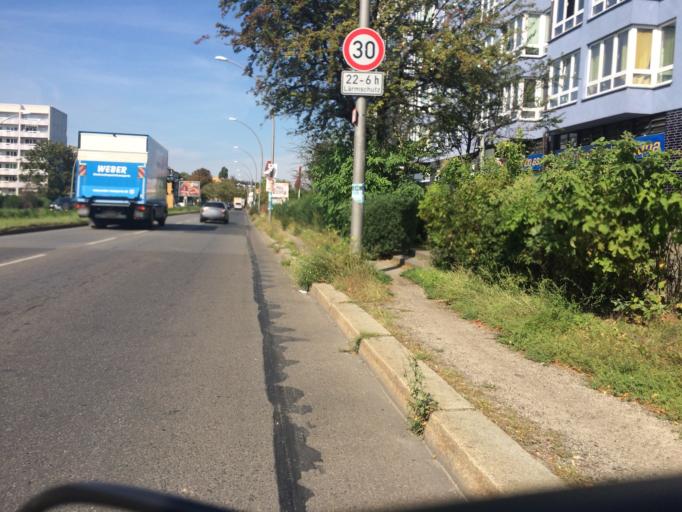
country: DE
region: Berlin
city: Heinersdorf
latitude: 52.5621
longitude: 13.4278
